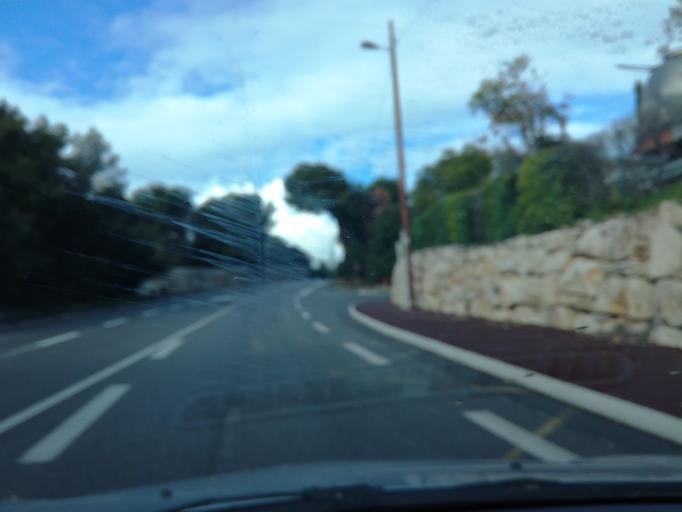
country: FR
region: Provence-Alpes-Cote d'Azur
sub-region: Departement des Alpes-Maritimes
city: Pegomas
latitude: 43.6238
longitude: 6.9356
